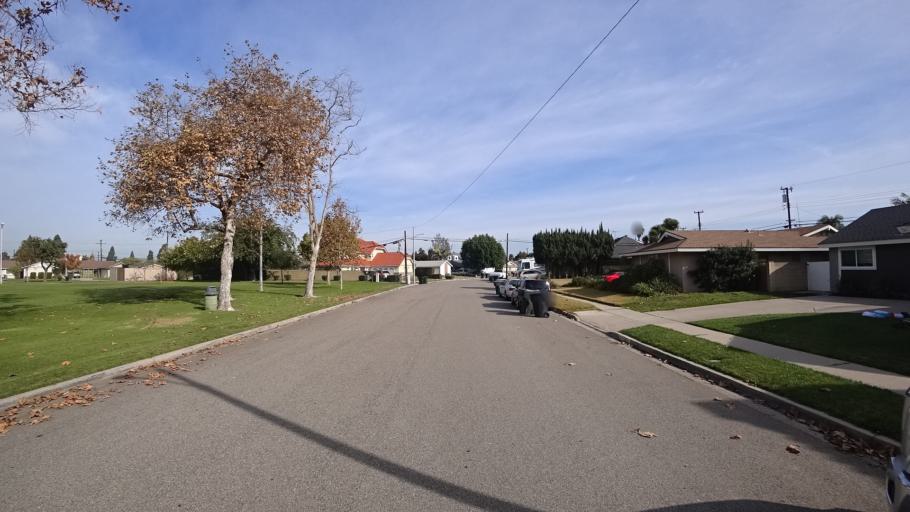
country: US
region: California
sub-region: Orange County
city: Cypress
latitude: 33.7803
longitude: -118.0372
